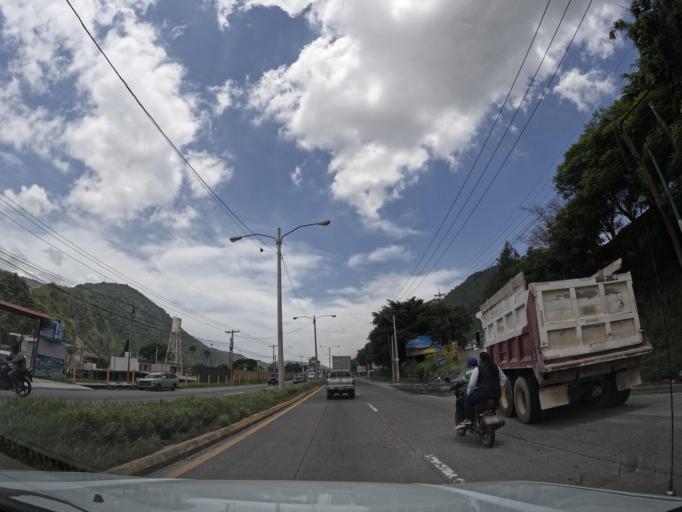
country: GT
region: Escuintla
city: San Vicente Pacaya
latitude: 14.4465
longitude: -90.6459
